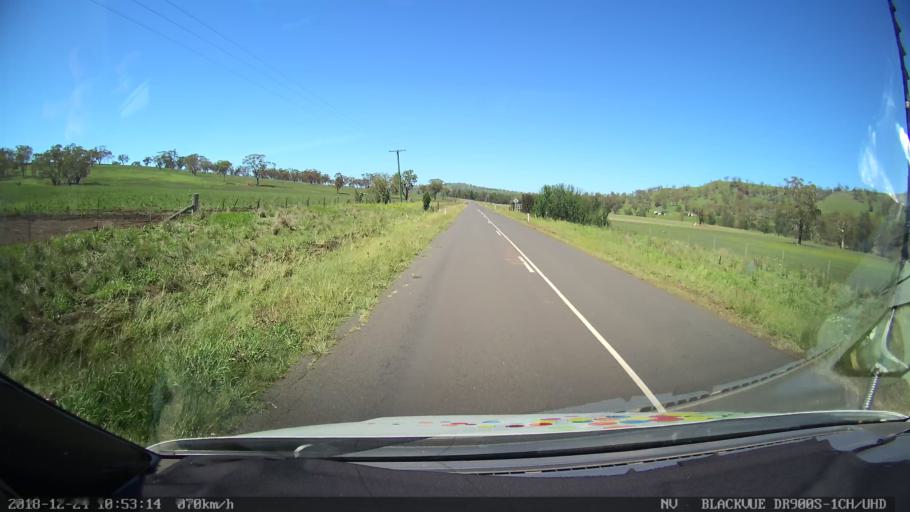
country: AU
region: New South Wales
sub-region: Upper Hunter Shire
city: Merriwa
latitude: -31.9894
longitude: 150.4223
